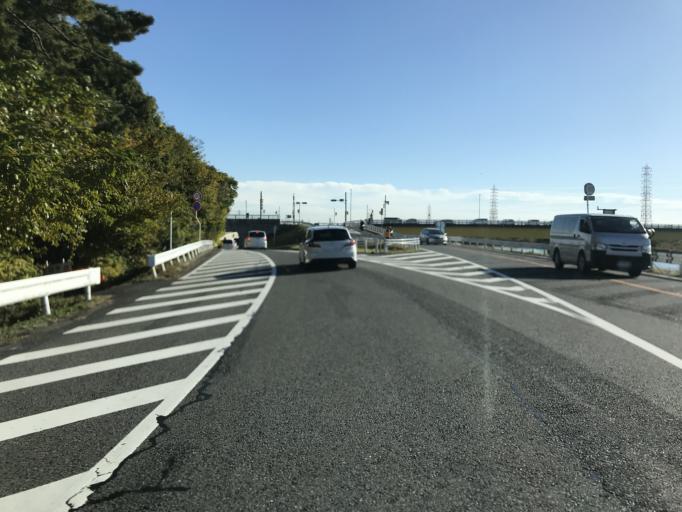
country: JP
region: Aichi
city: Kanie
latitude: 35.1485
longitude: 136.8305
